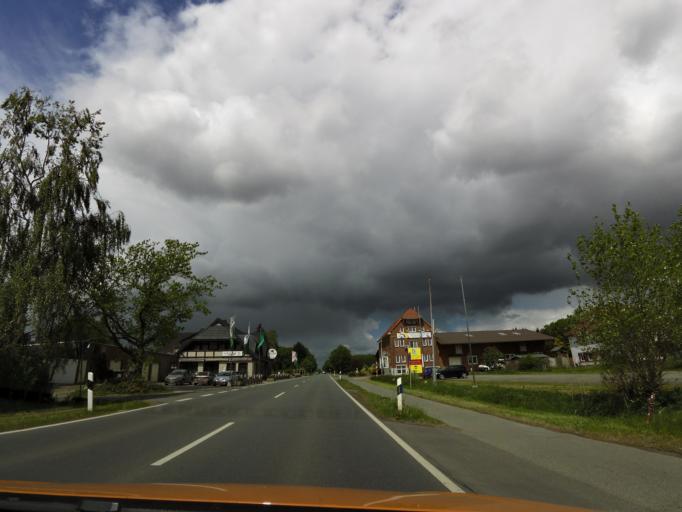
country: DE
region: Lower Saxony
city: Ganderkesee
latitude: 53.0638
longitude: 8.5292
